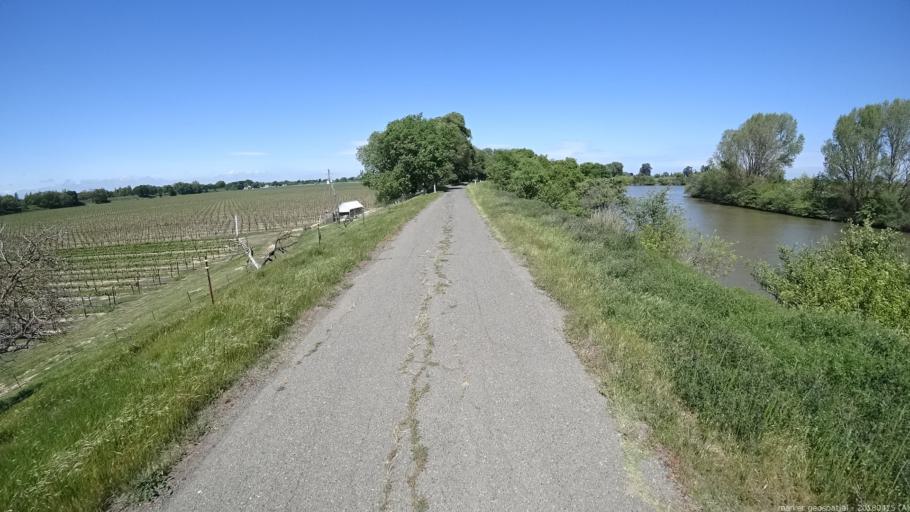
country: US
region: California
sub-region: Sacramento County
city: Walnut Grove
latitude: 38.2595
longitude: -121.5953
